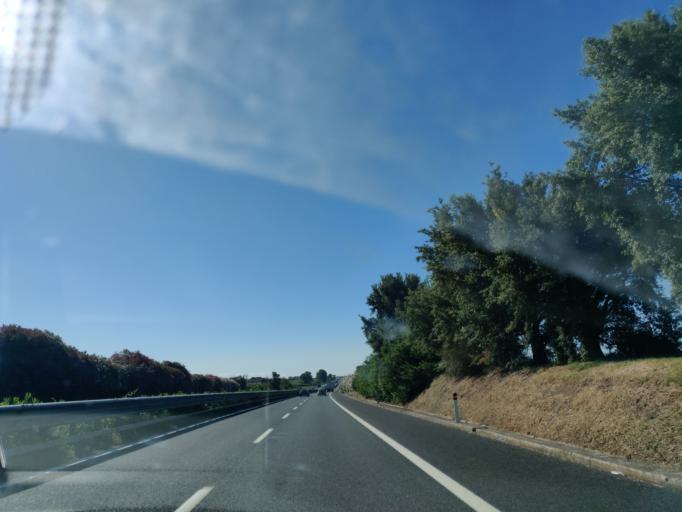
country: IT
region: Latium
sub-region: Citta metropolitana di Roma Capitale
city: Marina di Cerveteri
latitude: 41.9993
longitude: 12.0457
